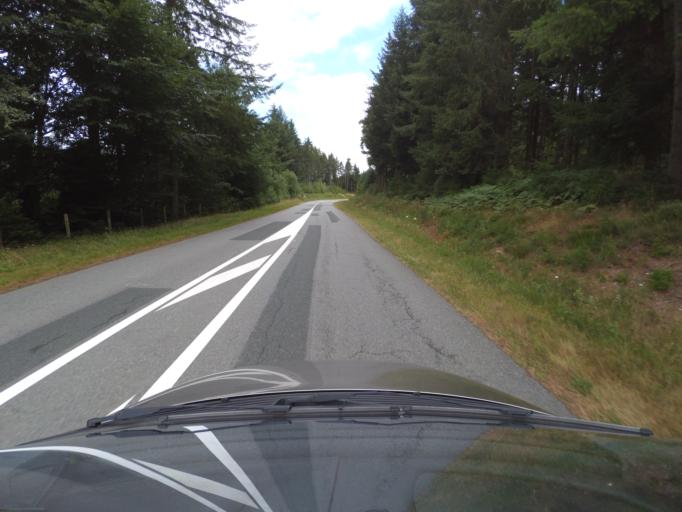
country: FR
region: Limousin
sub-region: Departement de la Haute-Vienne
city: Peyrat-le-Chateau
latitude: 45.8276
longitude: 1.9154
